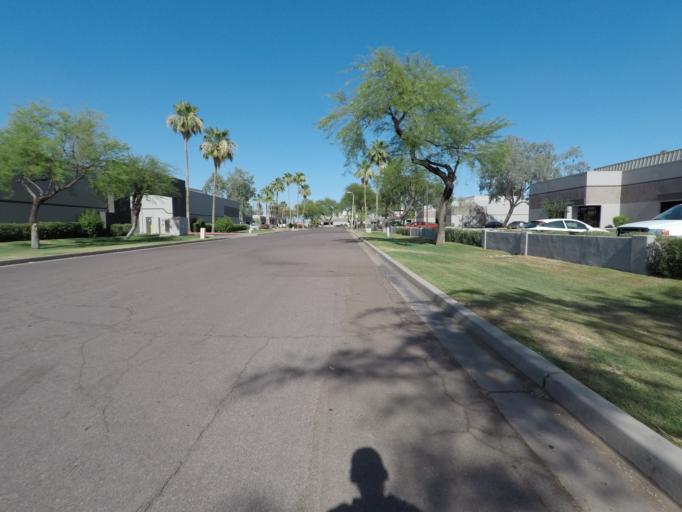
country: US
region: Arizona
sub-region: Maricopa County
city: Tempe Junction
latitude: 33.4158
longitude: -111.9765
